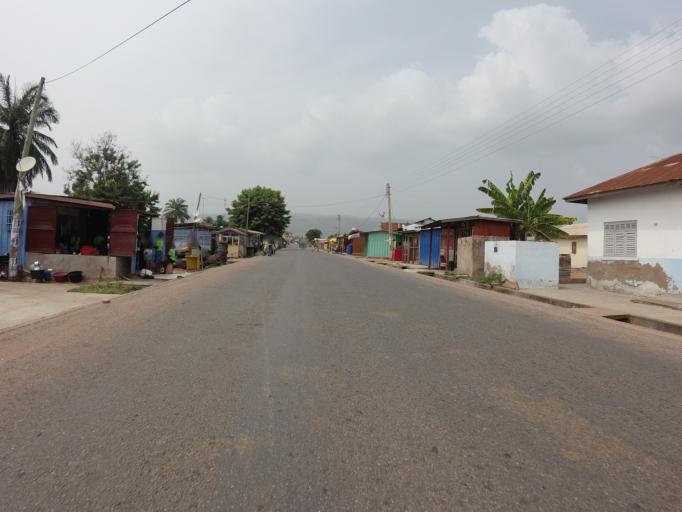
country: GH
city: Akropong
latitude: 6.1036
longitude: -0.0106
